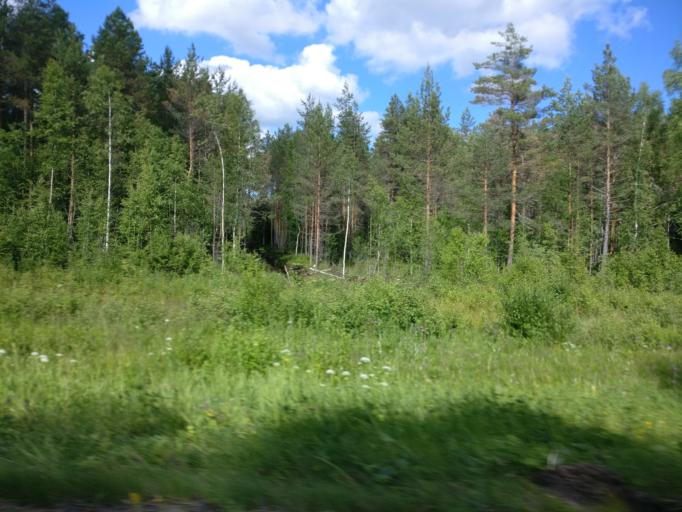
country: FI
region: Southern Savonia
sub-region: Savonlinna
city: Kerimaeki
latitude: 61.8570
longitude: 29.1604
